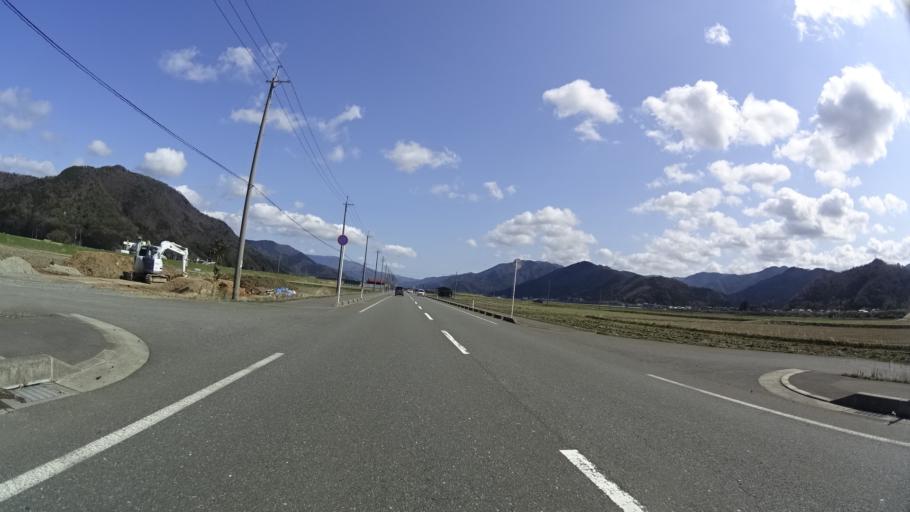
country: JP
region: Fukui
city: Obama
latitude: 35.4867
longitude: 135.7892
